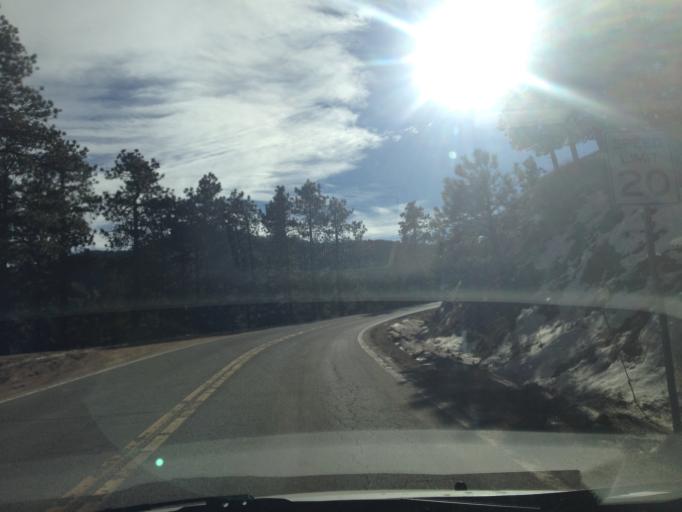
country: US
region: Colorado
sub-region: Boulder County
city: Boulder
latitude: 39.9944
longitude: -105.3102
